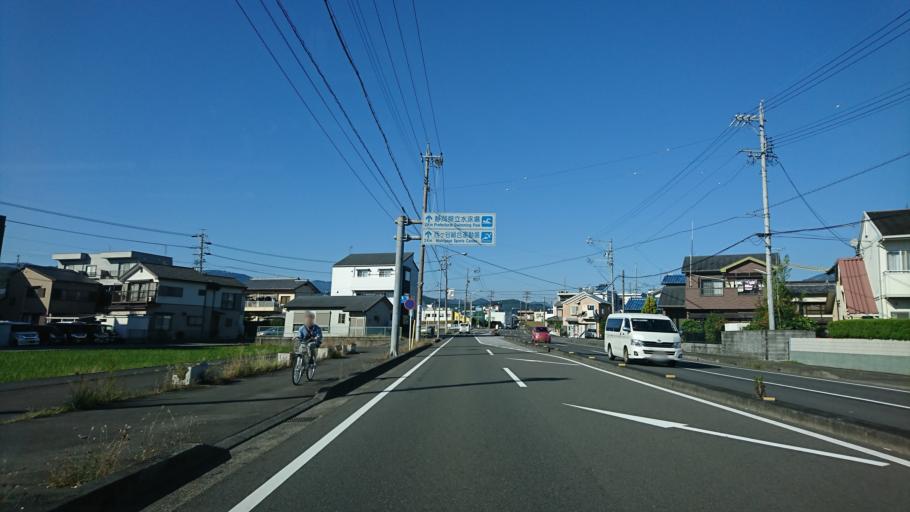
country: JP
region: Shizuoka
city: Shizuoka-shi
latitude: 34.9990
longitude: 138.3641
